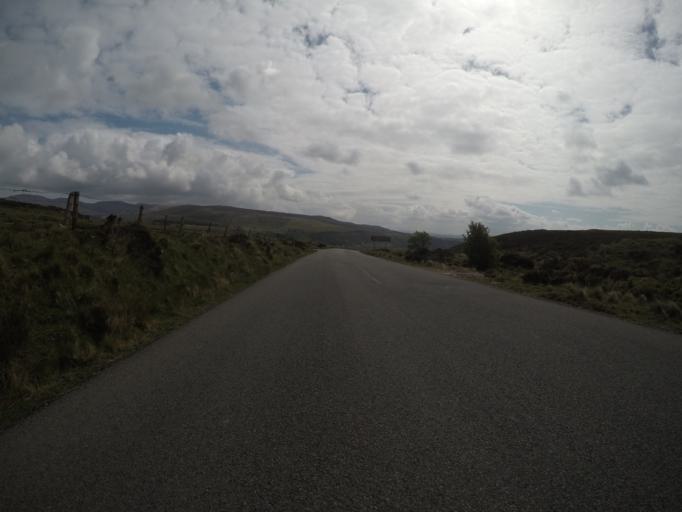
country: GB
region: Scotland
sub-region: Highland
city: Portree
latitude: 57.5946
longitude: -6.3734
